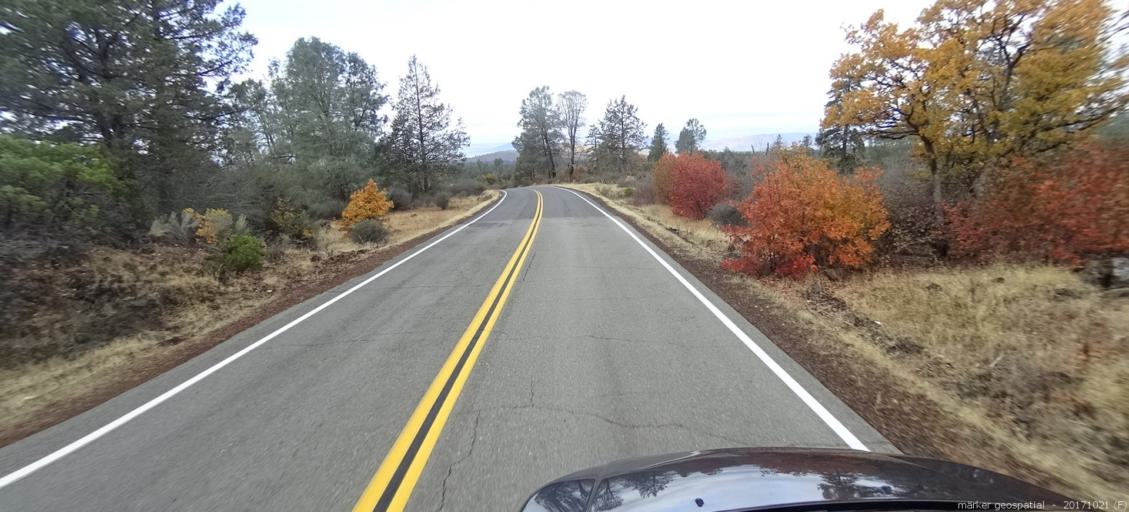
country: US
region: California
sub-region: Shasta County
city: Burney
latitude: 40.9193
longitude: -121.5061
